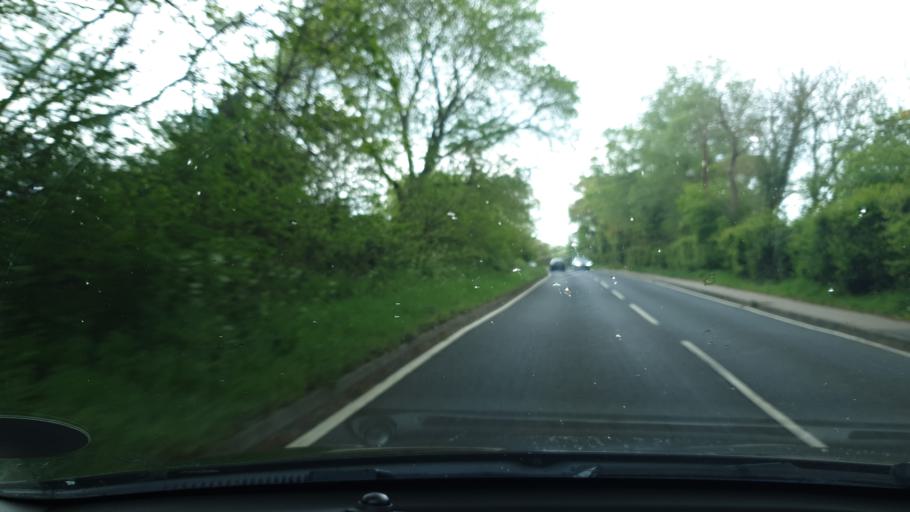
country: GB
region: England
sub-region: Essex
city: Little Clacton
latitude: 51.8517
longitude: 1.1634
